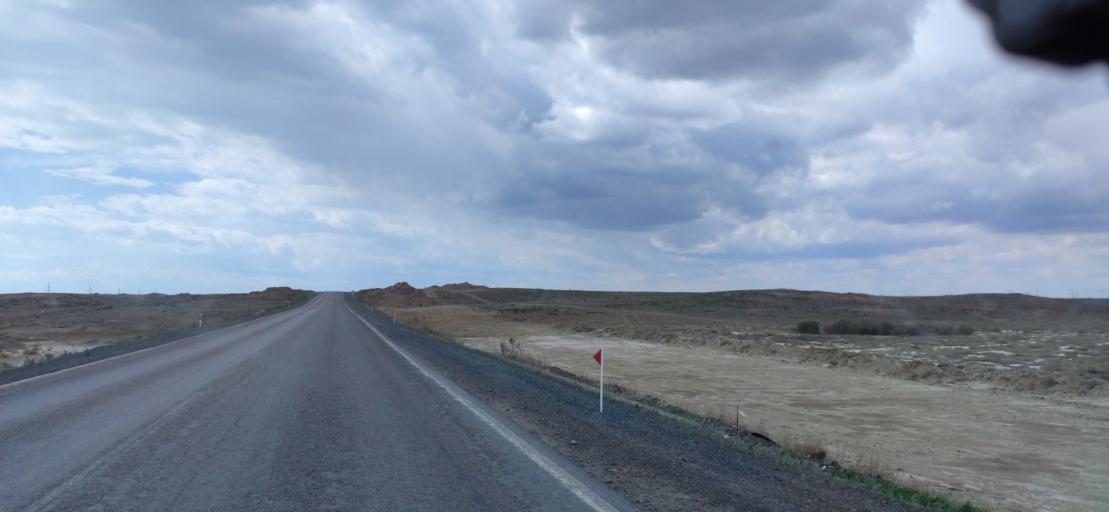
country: KZ
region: Qaraghandy
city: Saryshaghan
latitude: 46.0862
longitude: 73.6060
